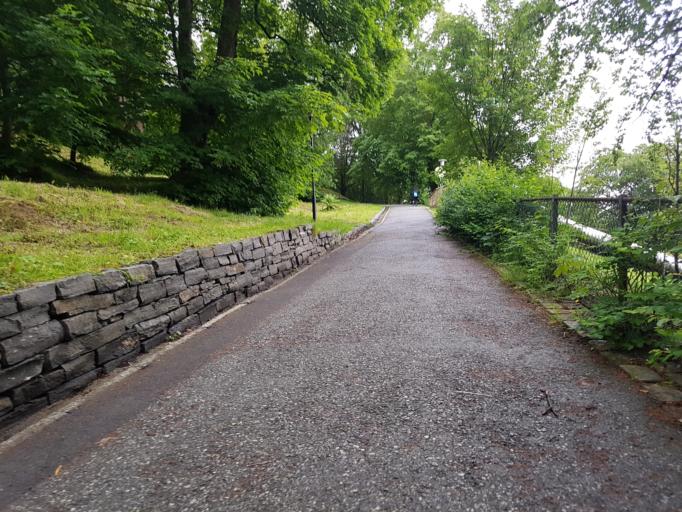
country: NO
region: Hordaland
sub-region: Bergen
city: Bergen
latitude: 60.3972
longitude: 5.3317
